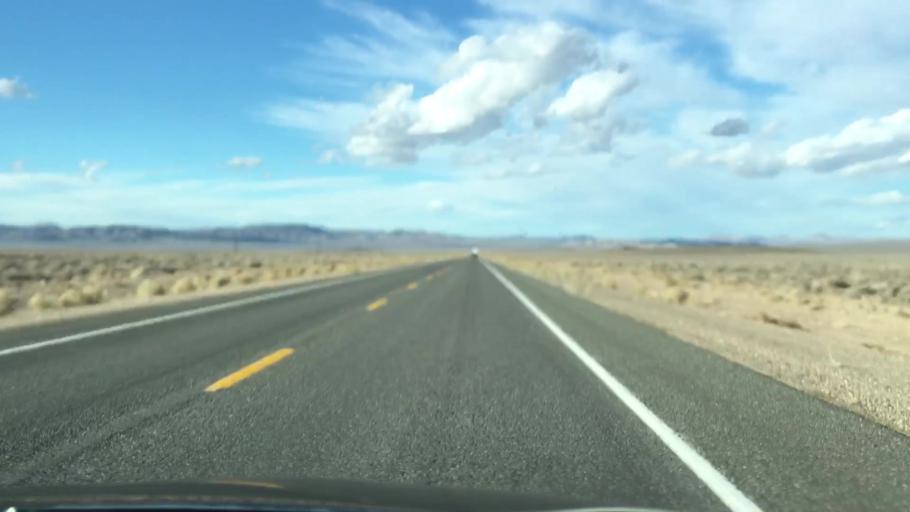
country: US
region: Nevada
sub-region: Esmeralda County
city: Goldfield
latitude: 37.4031
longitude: -117.1498
